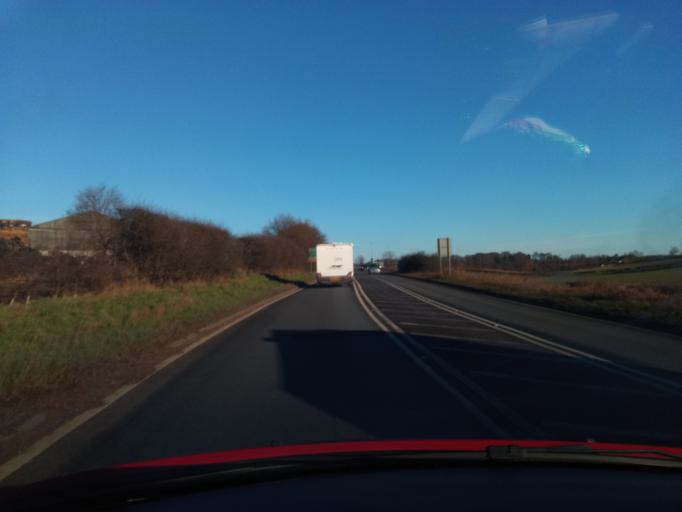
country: GB
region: England
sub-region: Nottinghamshire
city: Farnsfield
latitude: 53.1181
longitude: -1.0646
